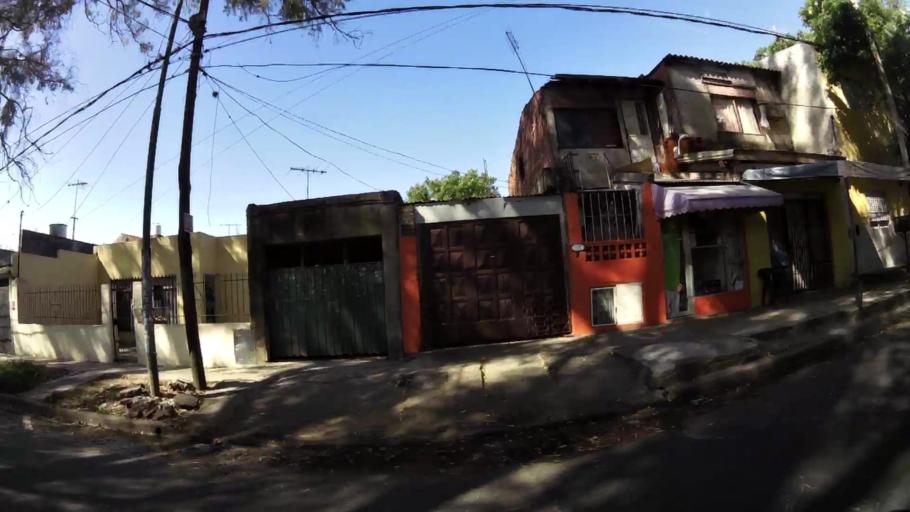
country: AR
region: Buenos Aires
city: Caseros
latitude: -34.5430
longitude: -58.5885
